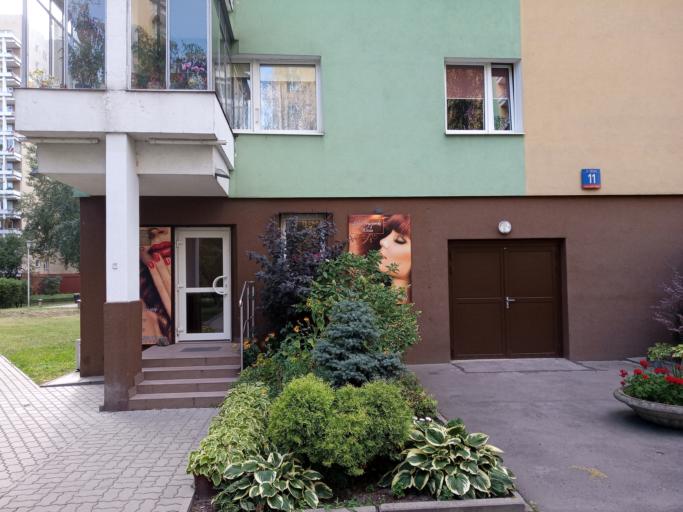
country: PL
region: Masovian Voivodeship
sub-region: Warszawa
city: Zoliborz
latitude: 52.2794
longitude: 20.9826
